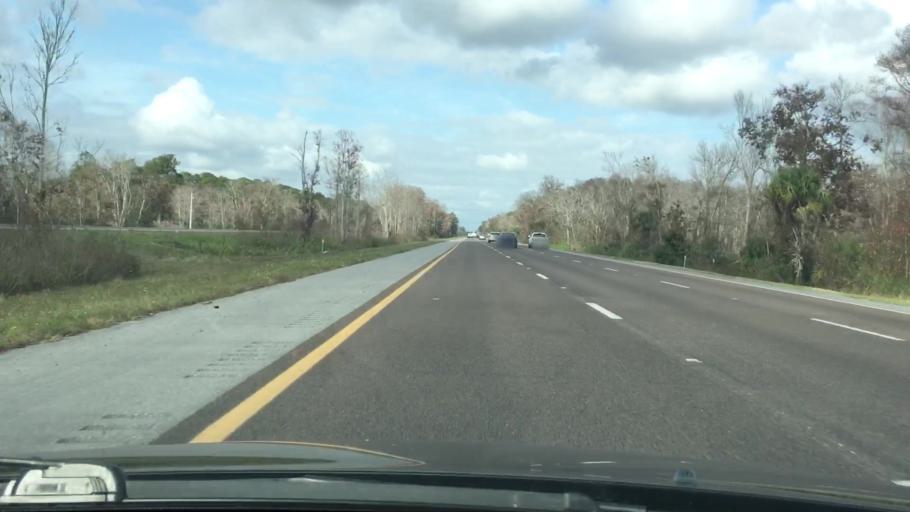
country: US
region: Florida
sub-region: Volusia County
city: Oak Hill
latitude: 28.8737
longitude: -80.9204
